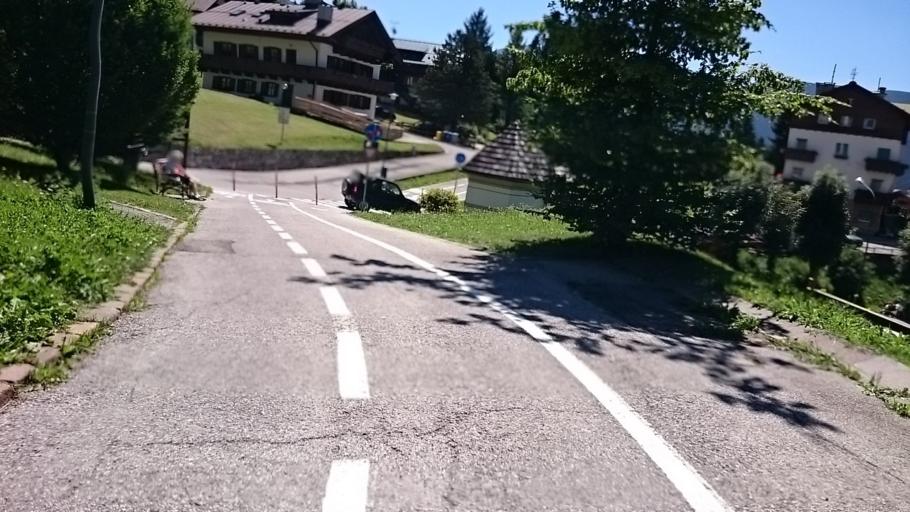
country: IT
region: Veneto
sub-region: Provincia di Belluno
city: San Vito
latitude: 46.4596
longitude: 12.2063
